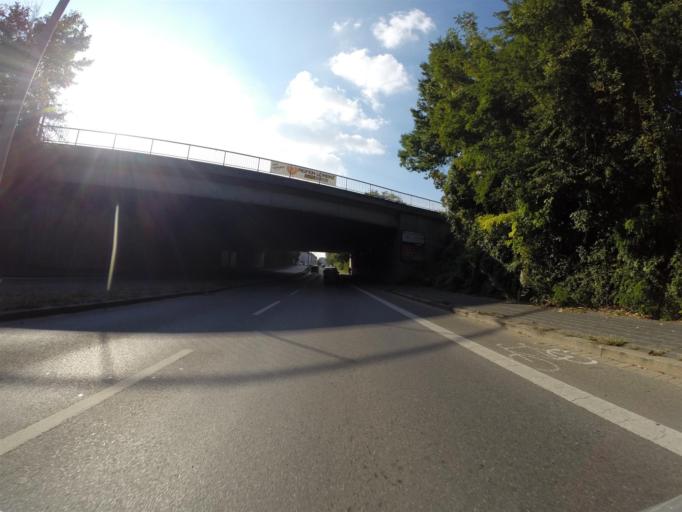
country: DE
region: Bavaria
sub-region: Regierungsbezirk Mittelfranken
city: Nuernberg
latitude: 49.4696
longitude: 11.0778
